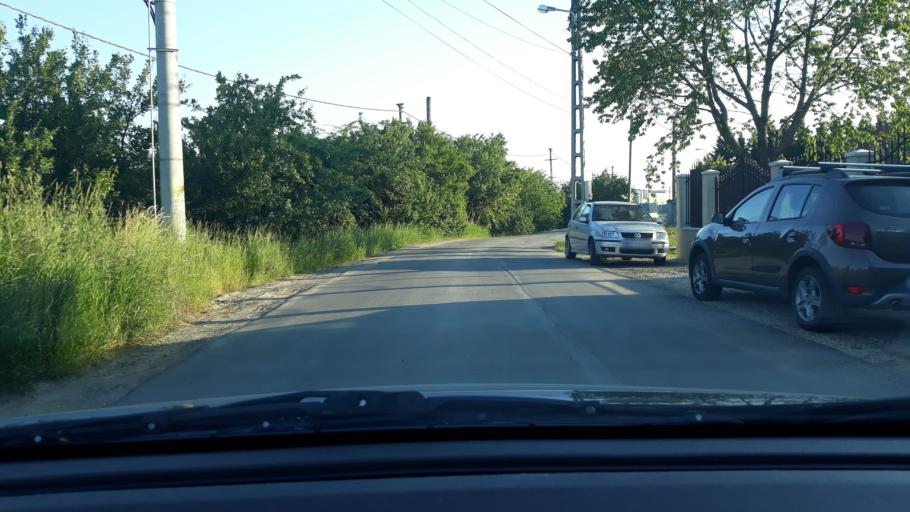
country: RO
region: Bihor
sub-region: Comuna Biharea
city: Oradea
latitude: 47.0963
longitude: 21.9304
